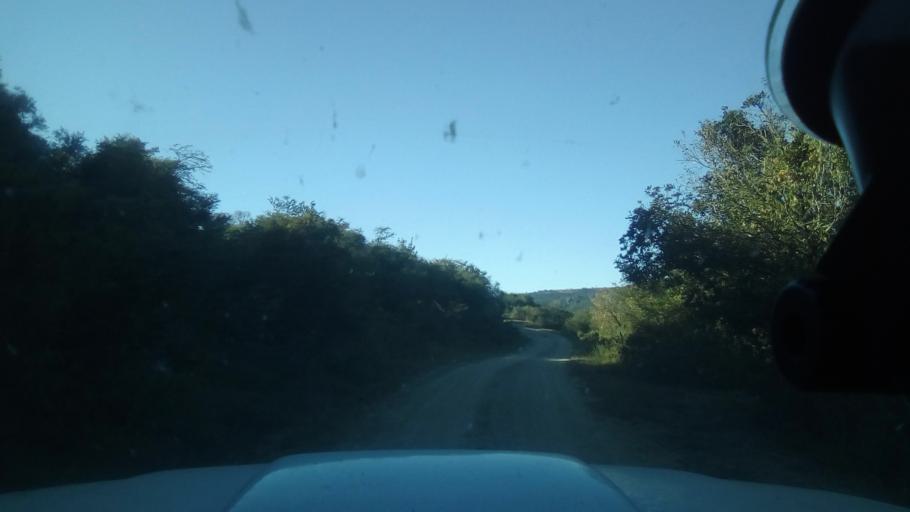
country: ZA
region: Eastern Cape
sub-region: Buffalo City Metropolitan Municipality
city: Bhisho
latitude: -32.7346
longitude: 27.3463
